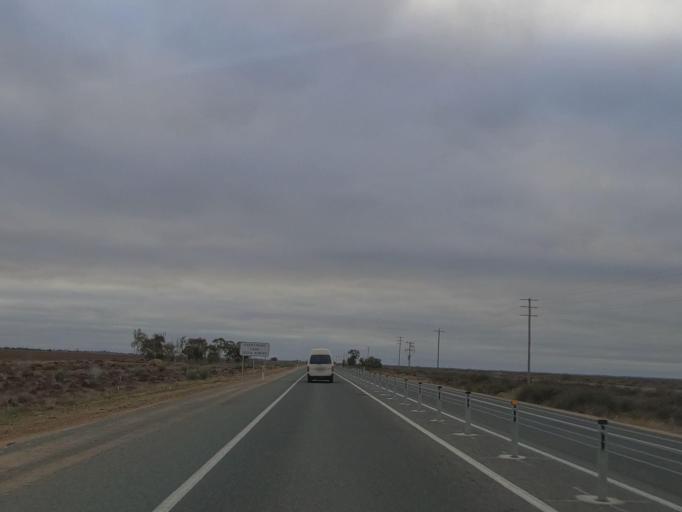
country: AU
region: Victoria
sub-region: Swan Hill
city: Swan Hill
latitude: -35.5194
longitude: 143.7304
